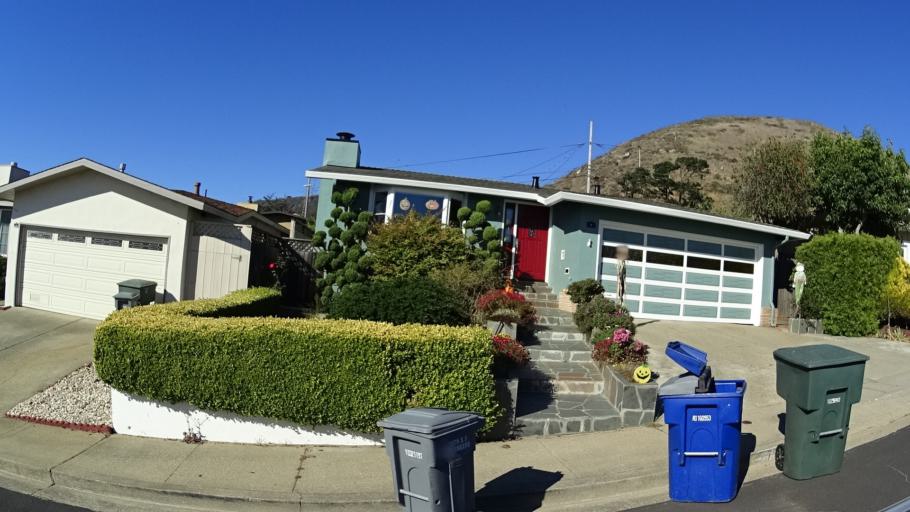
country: US
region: California
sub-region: San Mateo County
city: South San Francisco
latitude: 37.6678
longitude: -122.4323
